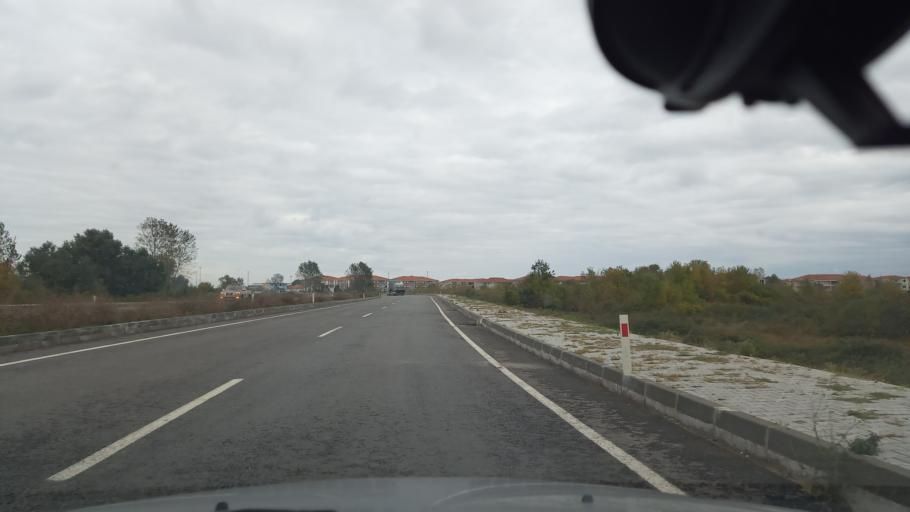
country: TR
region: Sakarya
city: Karasu
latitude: 41.1136
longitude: 30.6629
